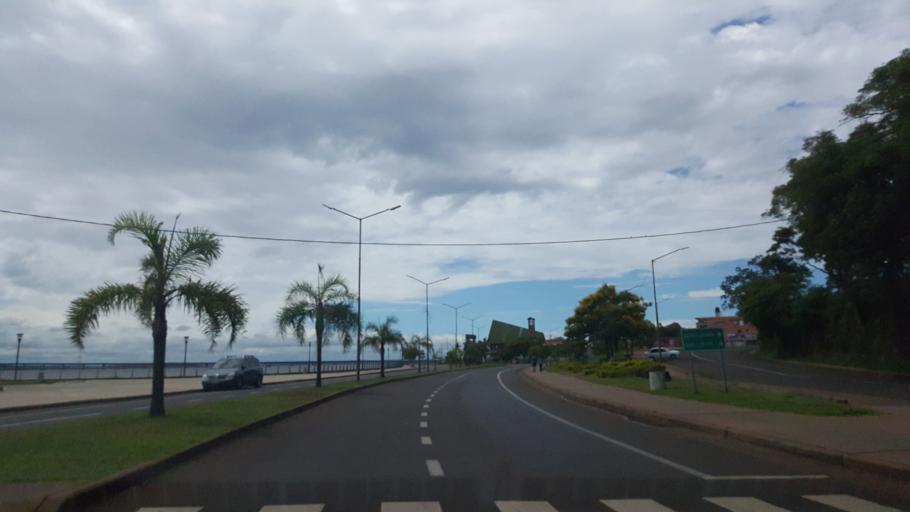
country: AR
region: Misiones
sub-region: Departamento de Capital
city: Posadas
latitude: -27.3623
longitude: -55.8867
